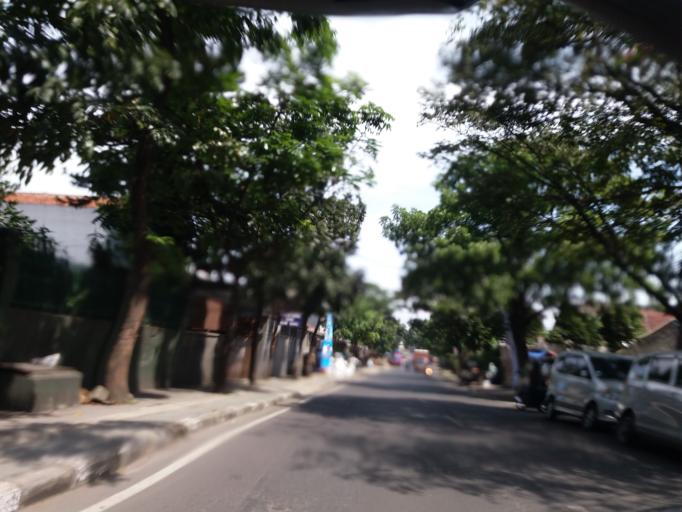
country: ID
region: West Java
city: Margahayukencana
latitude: -6.9290
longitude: 107.5737
